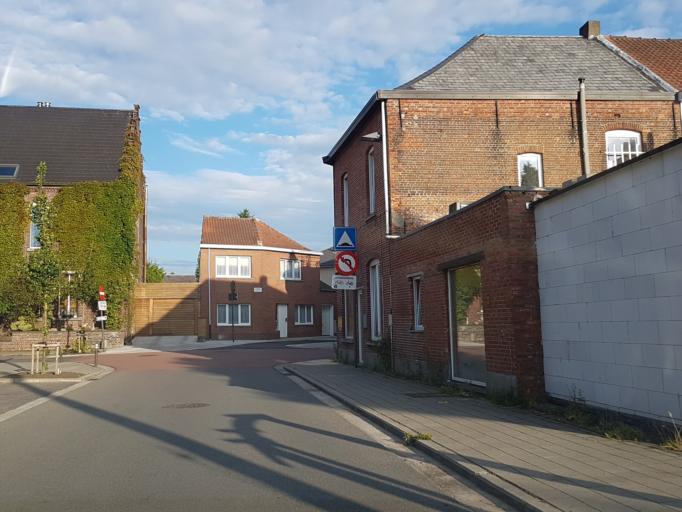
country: BE
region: Flanders
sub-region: Provincie Oost-Vlaanderen
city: Aalst
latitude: 50.9497
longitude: 4.0979
